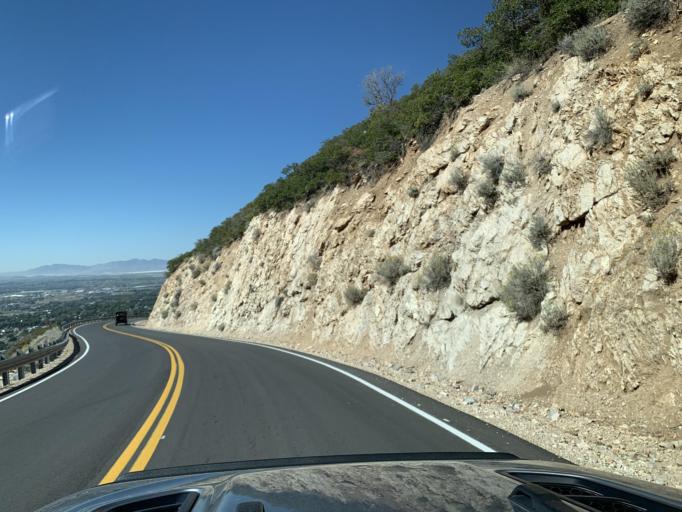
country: US
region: Utah
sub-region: Weber County
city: North Ogden
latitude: 41.3125
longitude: -111.9256
